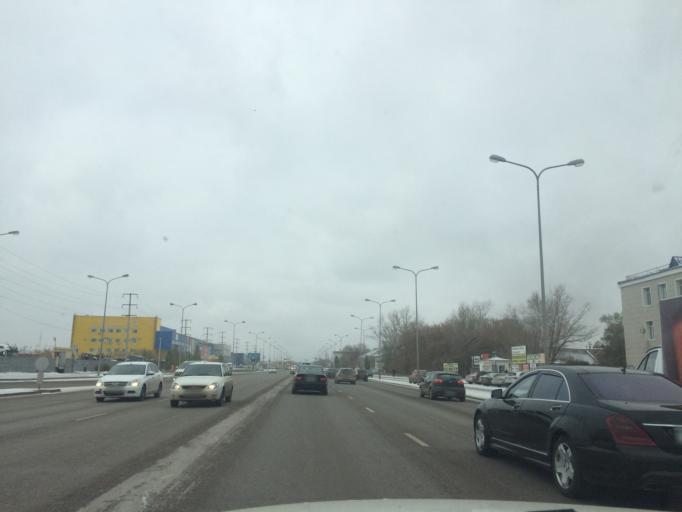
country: KZ
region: Astana Qalasy
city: Astana
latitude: 51.1813
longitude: 71.4612
